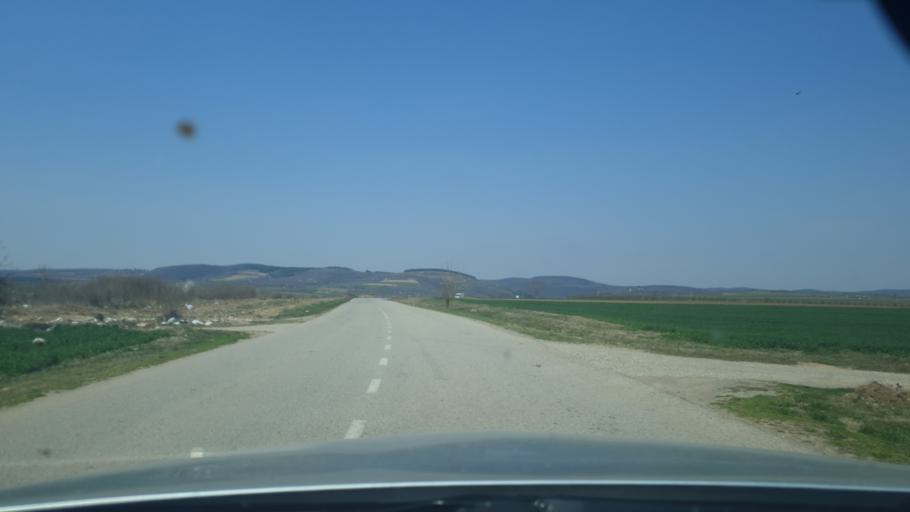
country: RS
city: Vrdnik
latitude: 45.0830
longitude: 19.7697
